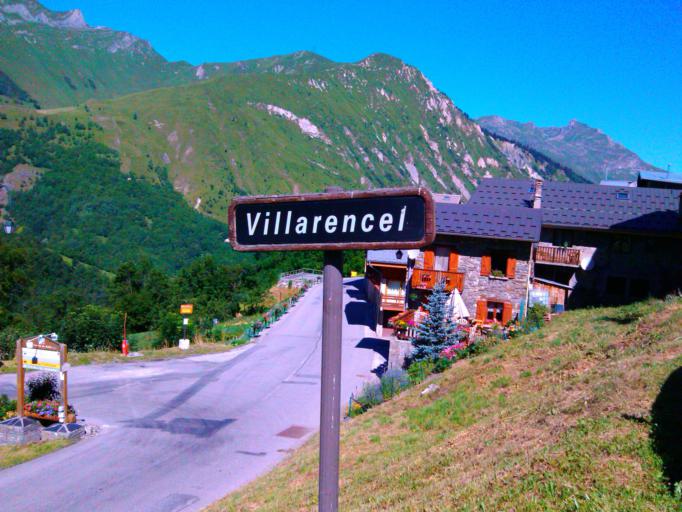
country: FR
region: Rhone-Alpes
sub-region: Departement de la Savoie
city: Saint-Martin-de-Belleville
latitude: 45.3814
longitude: 6.5034
